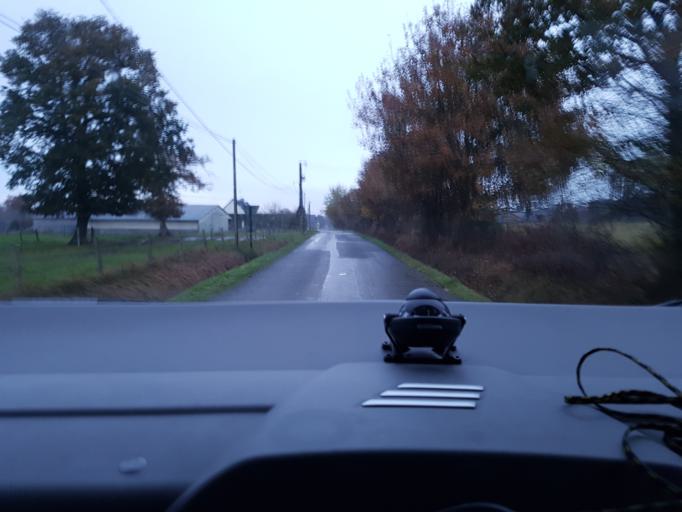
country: FR
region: Brittany
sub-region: Departement d'Ille-et-Vilaine
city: Saint-Aubin-du-Cormier
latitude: 48.2522
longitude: -1.3717
